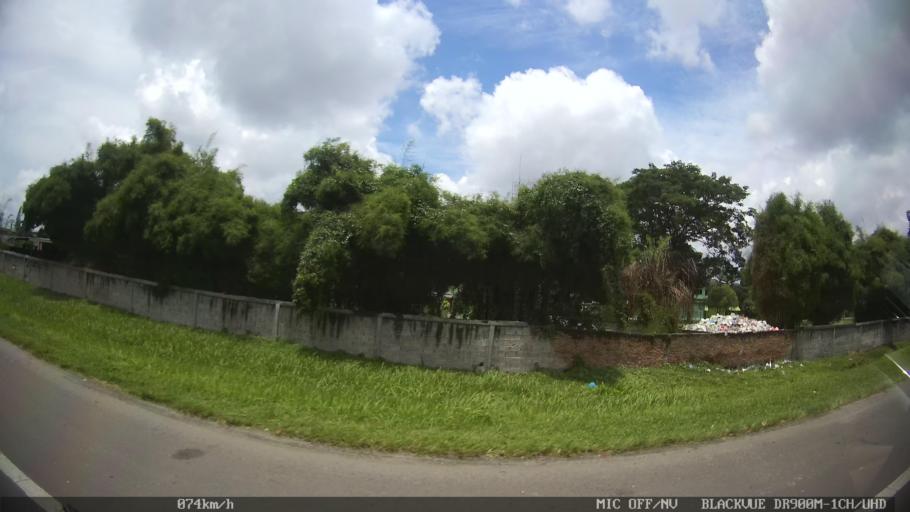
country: ID
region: North Sumatra
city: Medan
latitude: 3.6030
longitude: 98.7228
